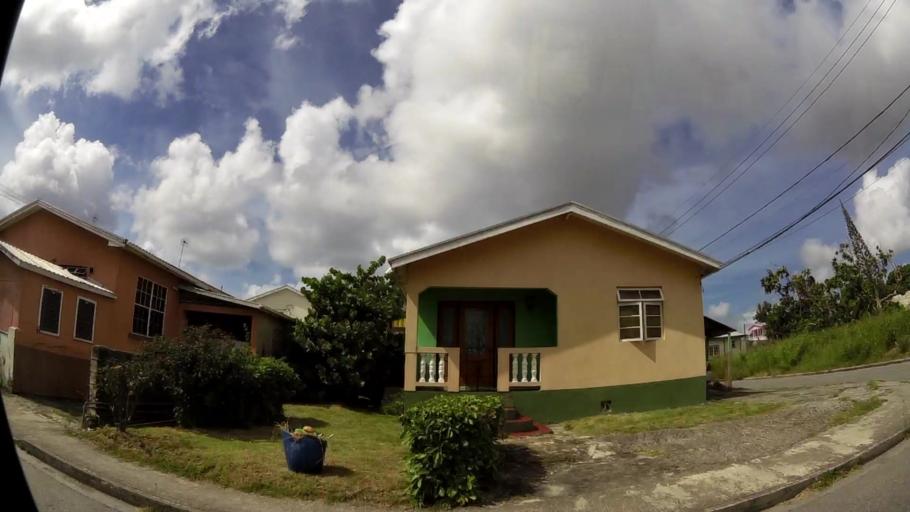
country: BB
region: Saint Michael
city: Bridgetown
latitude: 13.1225
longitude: -59.6156
